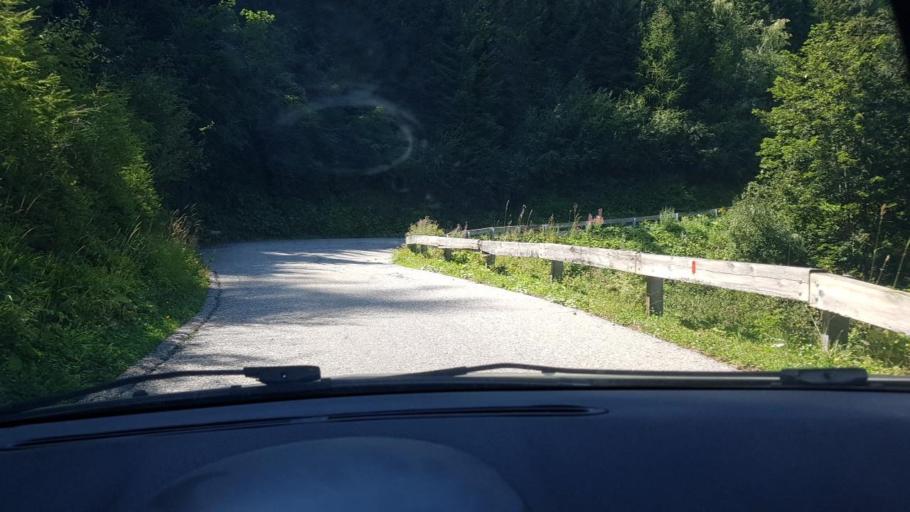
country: AT
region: Carinthia
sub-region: Politischer Bezirk Volkermarkt
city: Bad Eisenkappel
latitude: 46.4245
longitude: 14.5745
